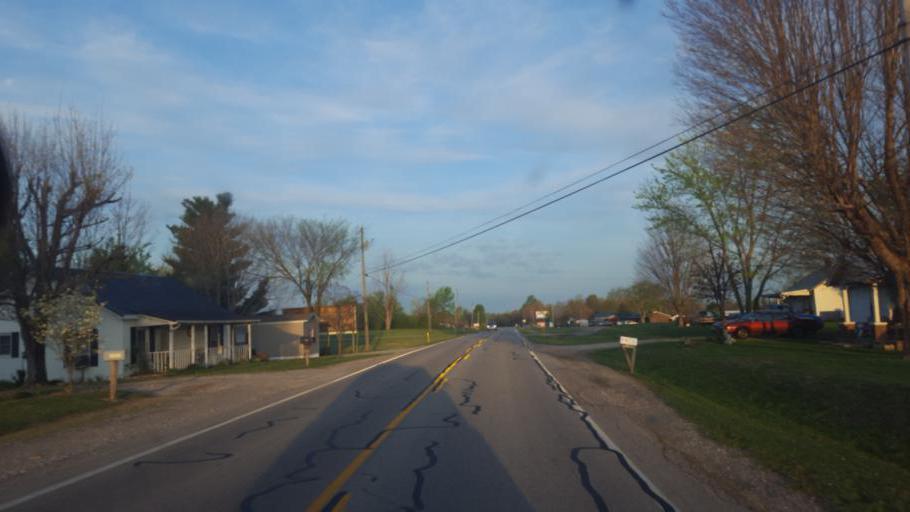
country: US
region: Kentucky
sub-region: Barren County
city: Cave City
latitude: 37.1324
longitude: -86.0156
